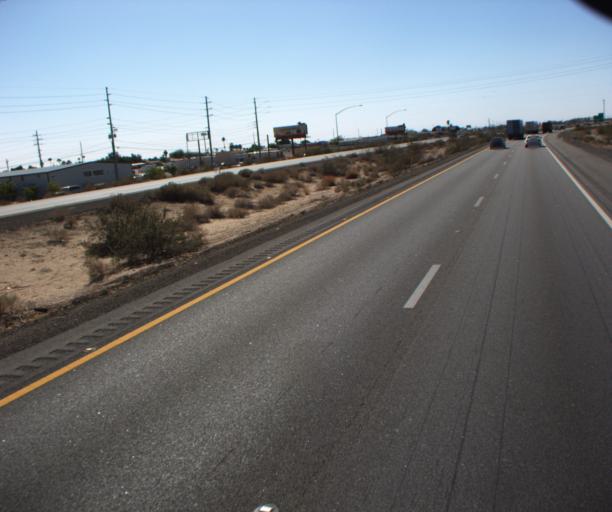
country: US
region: Arizona
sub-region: Yuma County
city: Fortuna Foothills
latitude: 32.6706
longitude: -114.4766
